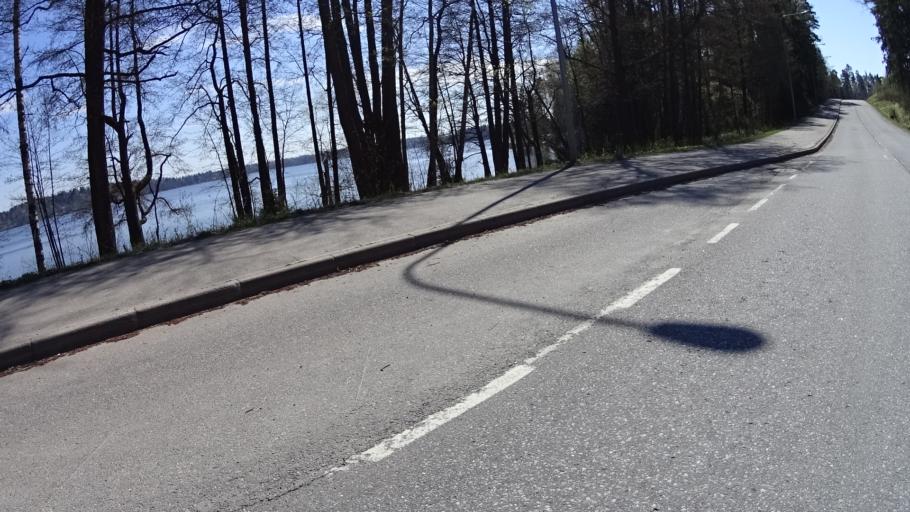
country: FI
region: Uusimaa
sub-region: Helsinki
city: Espoo
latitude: 60.2501
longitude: 24.6550
